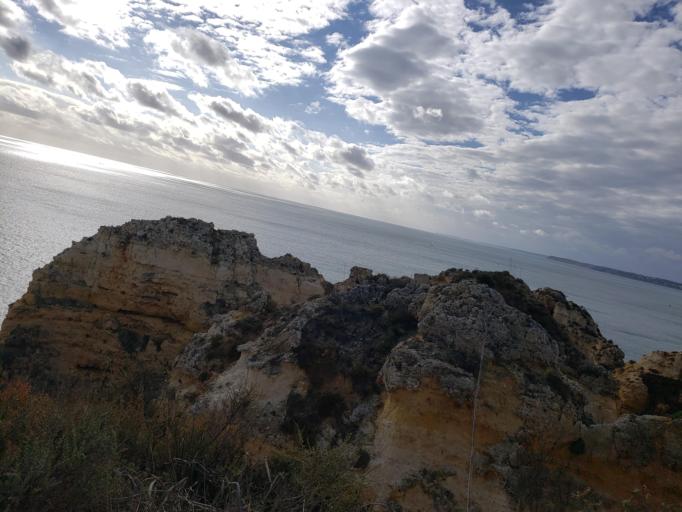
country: PT
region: Faro
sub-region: Lagos
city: Lagos
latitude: 37.0798
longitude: -8.6689
